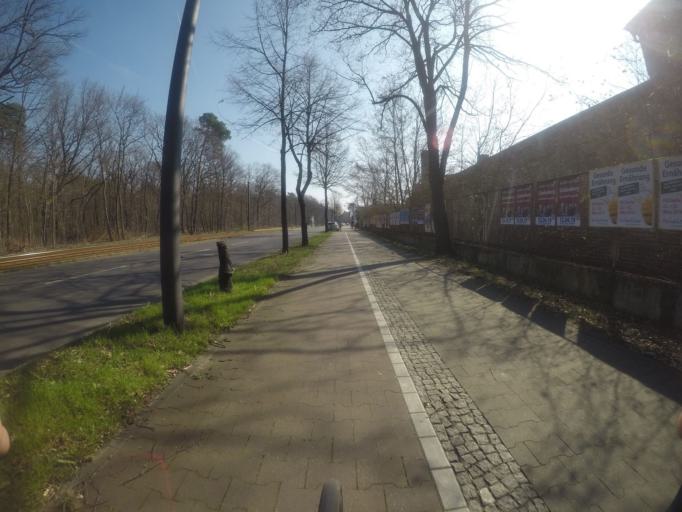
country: DE
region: Berlin
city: Friedrichshagen
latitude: 52.4494
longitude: 13.6075
